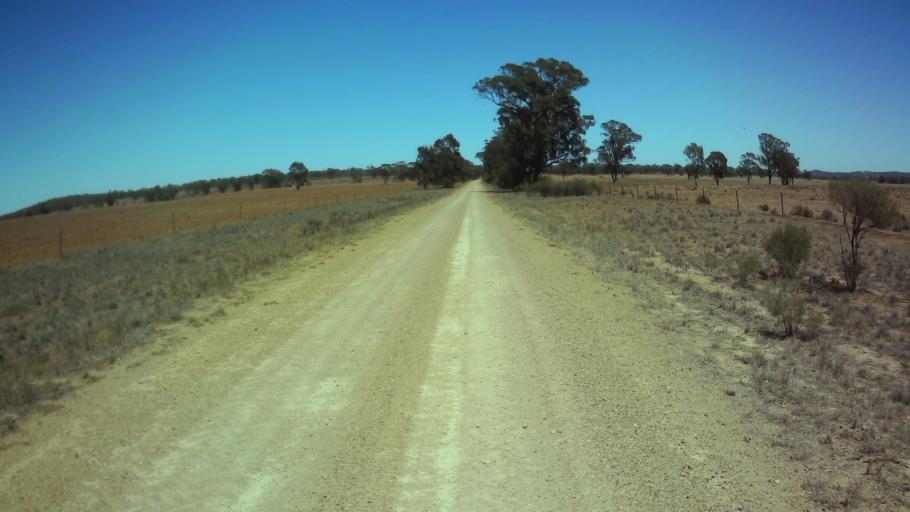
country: AU
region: New South Wales
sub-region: Forbes
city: Forbes
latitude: -33.6940
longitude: 147.8176
